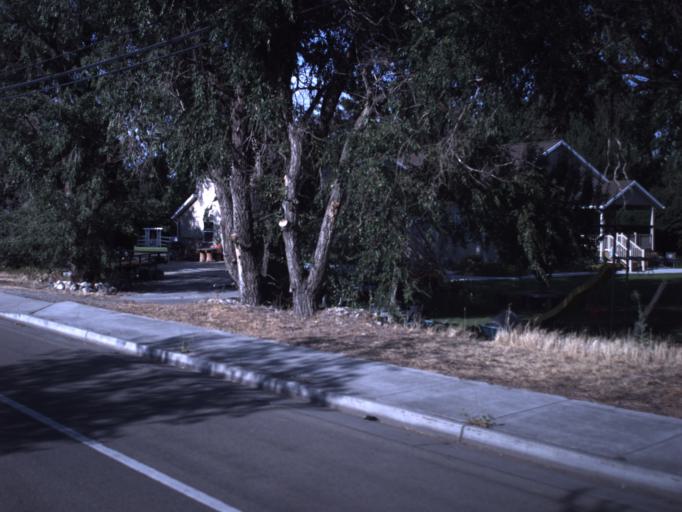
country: US
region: Utah
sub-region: Utah County
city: Alpine
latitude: 40.4256
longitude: -111.7859
